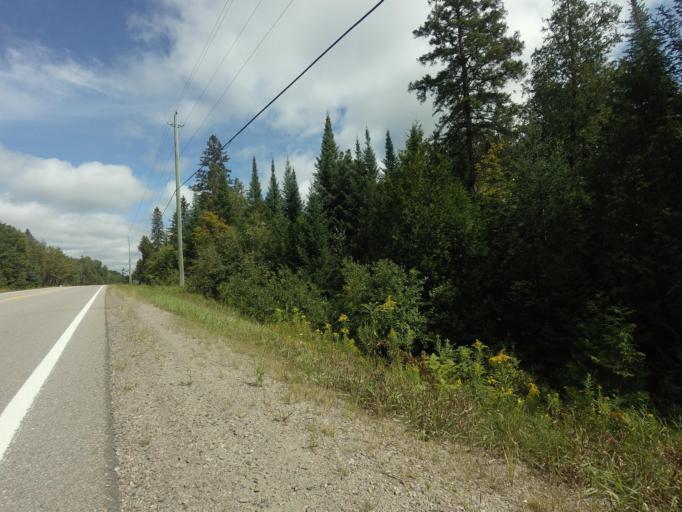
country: CA
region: Ontario
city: Omemee
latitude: 44.8321
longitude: -78.5593
